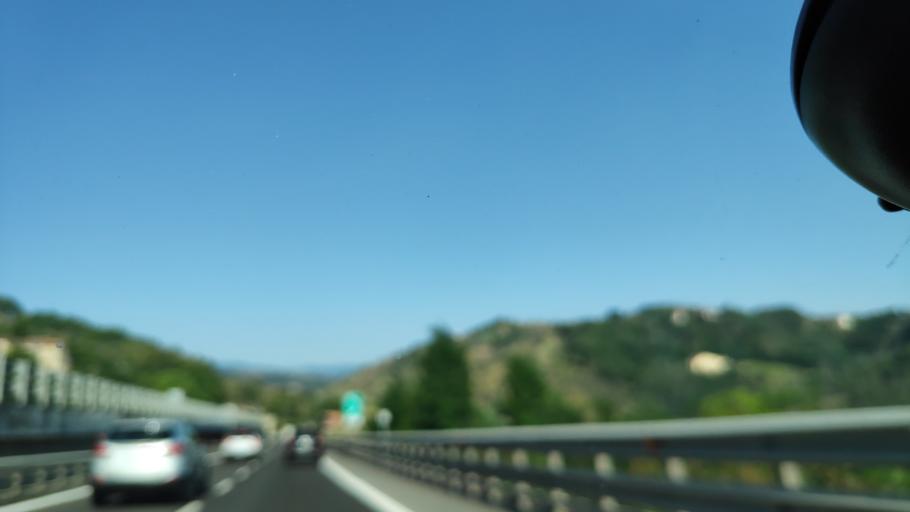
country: IT
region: Calabria
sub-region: Provincia di Cosenza
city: Donnici Inferiore
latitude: 39.2545
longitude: 16.2724
